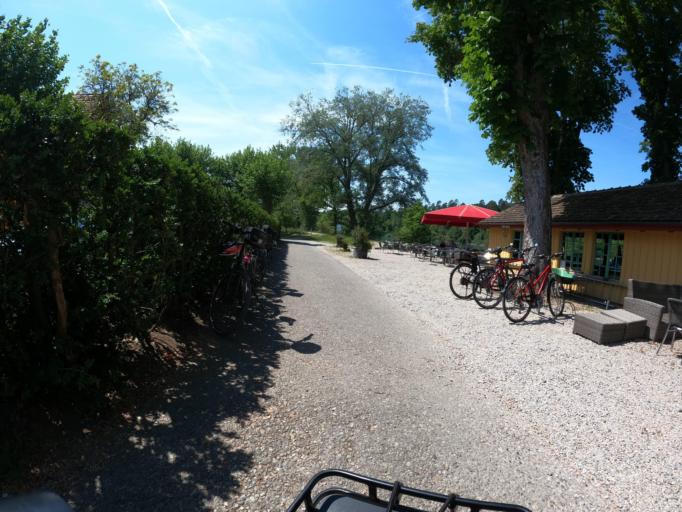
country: DE
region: Baden-Wuerttemberg
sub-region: Freiburg Region
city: Lottstetten
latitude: 47.6050
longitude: 8.5966
